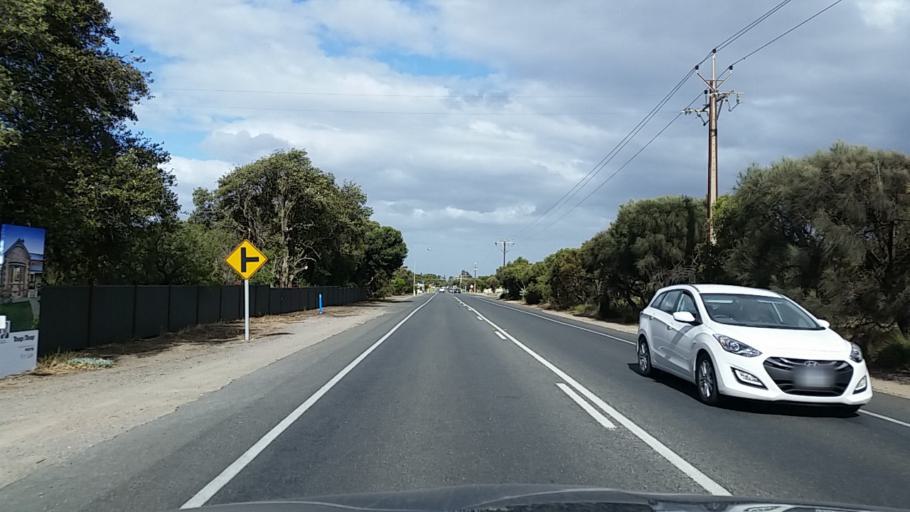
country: AU
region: South Australia
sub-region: Alexandrina
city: Goolwa
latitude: -35.5055
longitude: 138.7675
